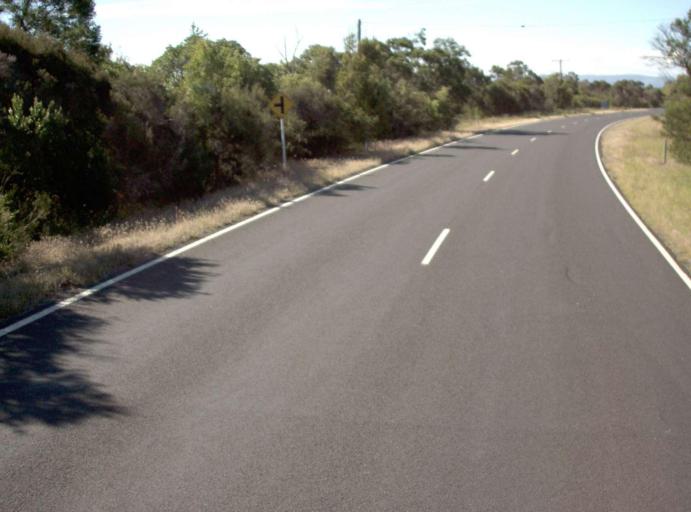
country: AU
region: Victoria
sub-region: Latrobe
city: Traralgon
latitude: -38.6438
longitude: 146.6715
